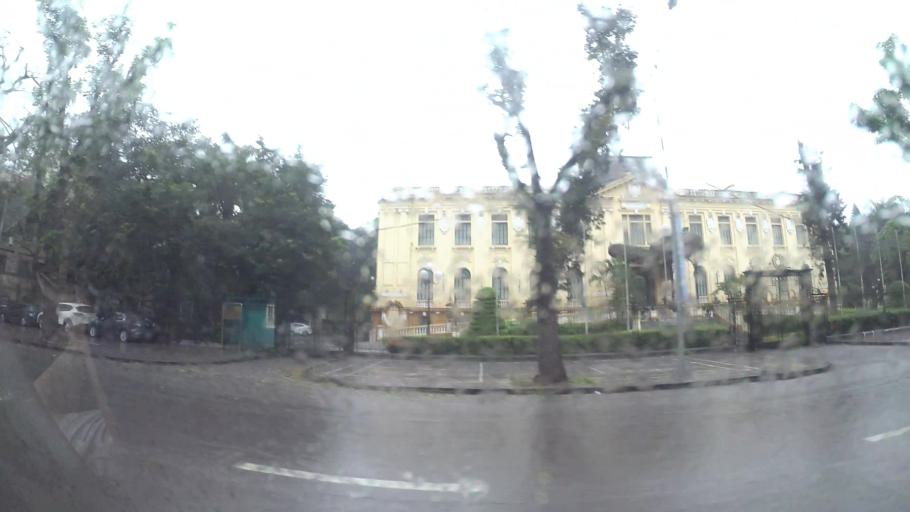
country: VN
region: Ha Noi
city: Hoan Kiem
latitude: 21.0264
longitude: 105.8557
